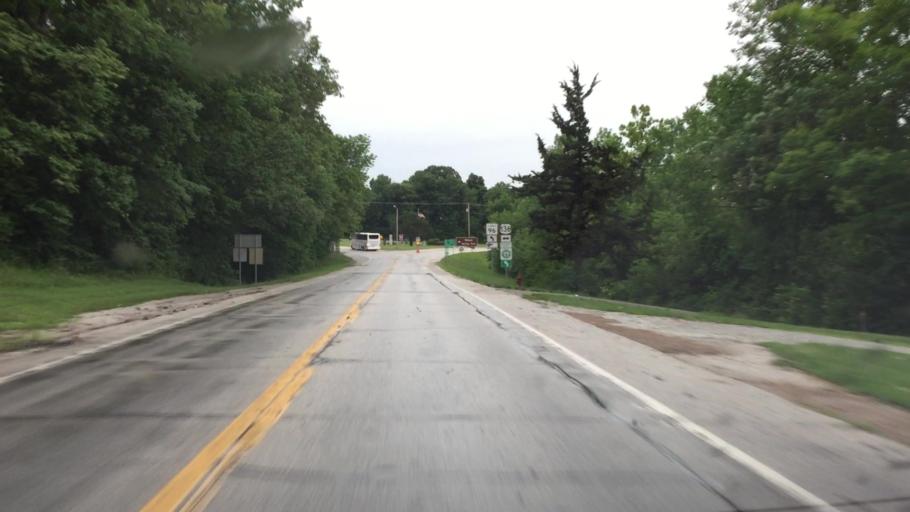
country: US
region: Illinois
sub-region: Hancock County
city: Hamilton
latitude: 40.3991
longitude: -91.3518
